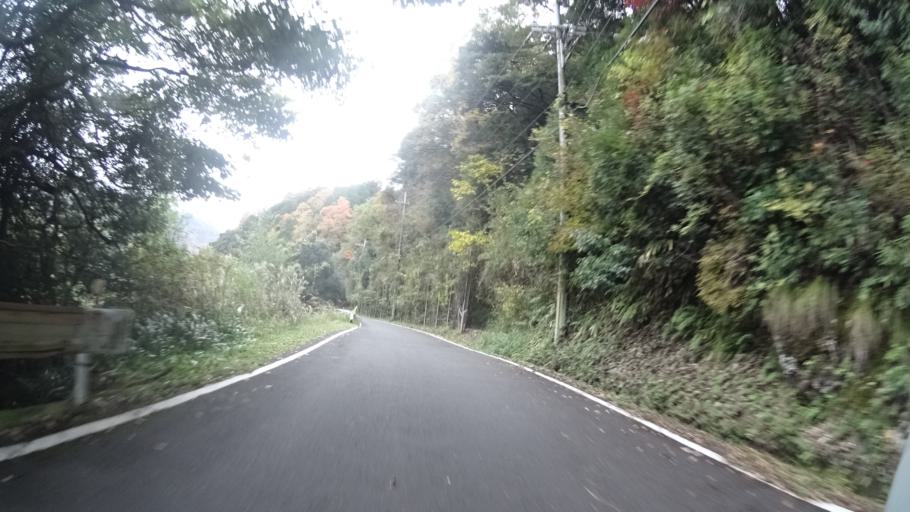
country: JP
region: Kyoto
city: Maizuru
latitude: 35.4962
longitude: 135.4661
